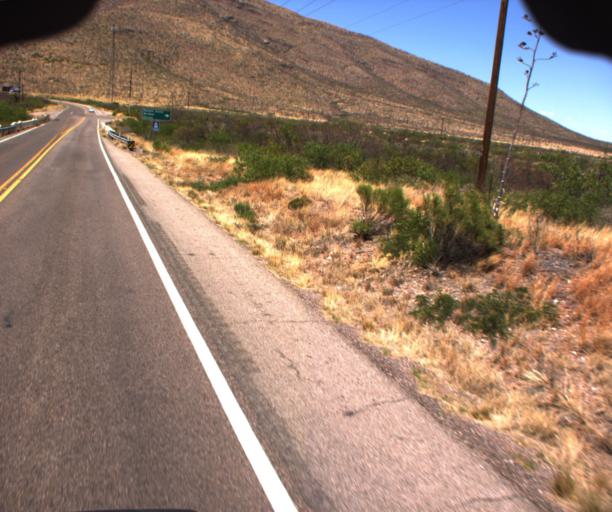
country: US
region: Arizona
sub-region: Cochise County
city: Bisbee
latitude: 31.4415
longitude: -109.8247
